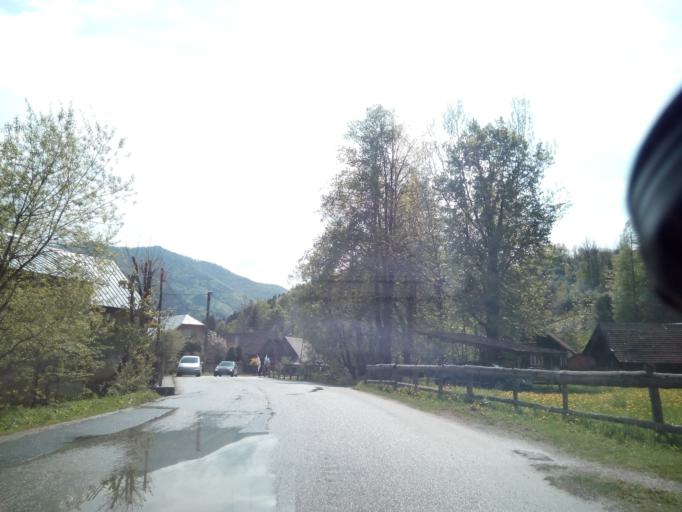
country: SK
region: Zilinsky
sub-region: Okres Zilina
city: Terchova
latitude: 49.2666
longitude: 19.0349
